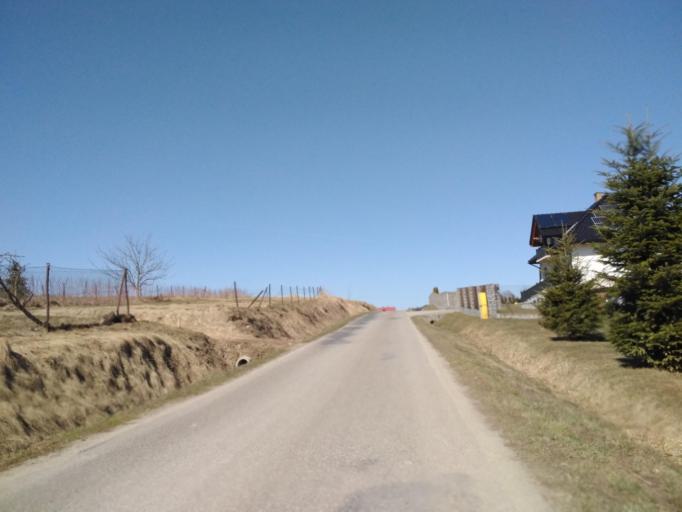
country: PL
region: Subcarpathian Voivodeship
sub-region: Powiat brzozowski
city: Orzechowka
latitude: 49.7154
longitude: 21.9650
